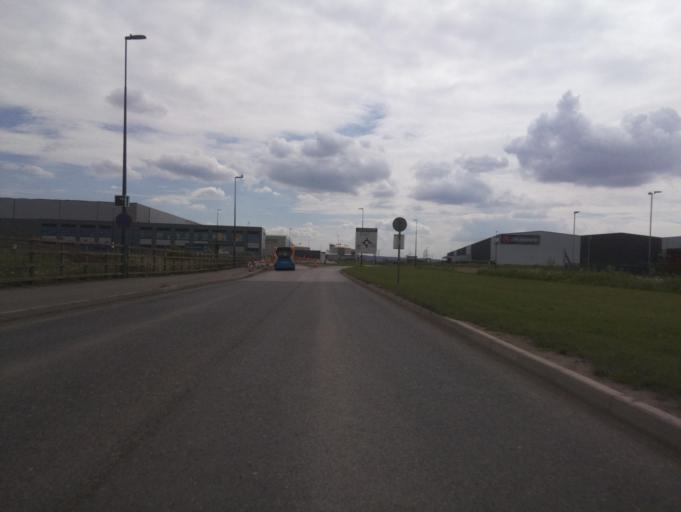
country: GB
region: England
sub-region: South Gloucestershire
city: Severn Beach
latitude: 51.5421
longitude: -2.6464
